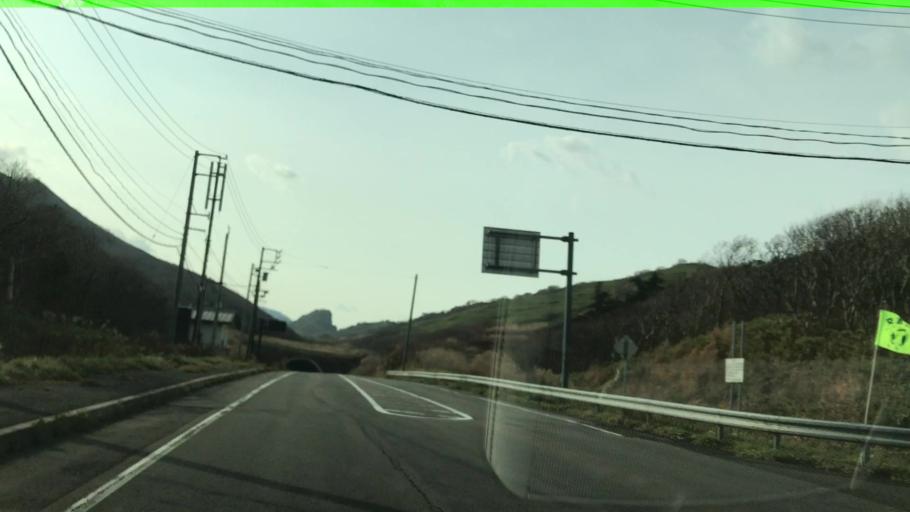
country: JP
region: Hokkaido
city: Iwanai
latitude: 43.3239
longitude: 140.3637
